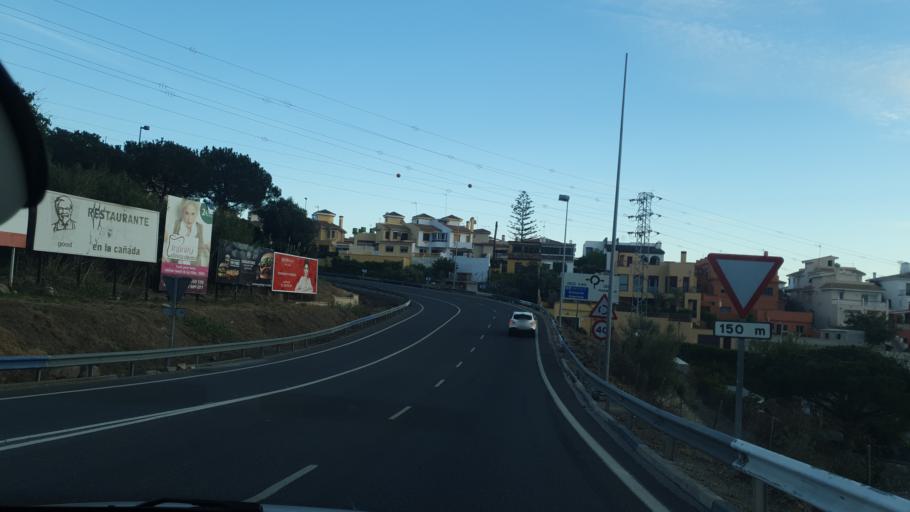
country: ES
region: Andalusia
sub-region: Provincia de Malaga
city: Marbella
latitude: 36.5199
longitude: -4.8817
